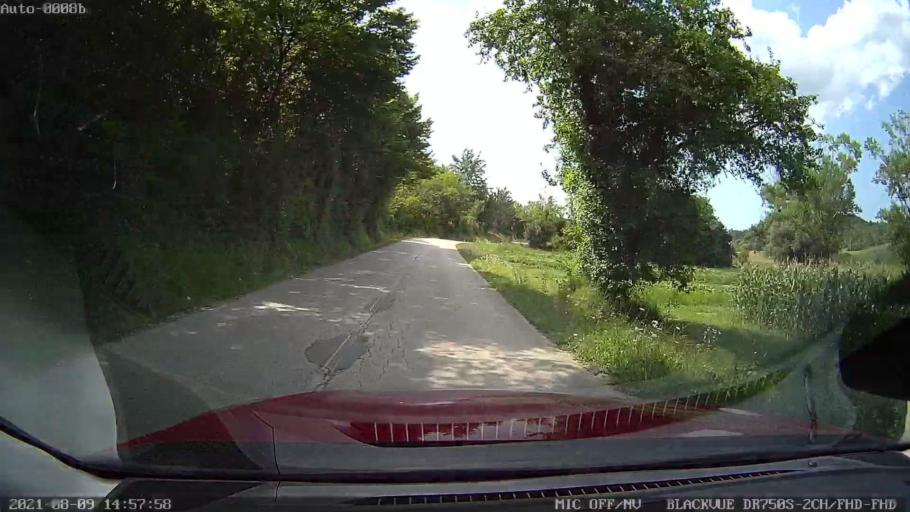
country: HR
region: Istarska
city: Pazin
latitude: 45.2646
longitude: 14.0456
